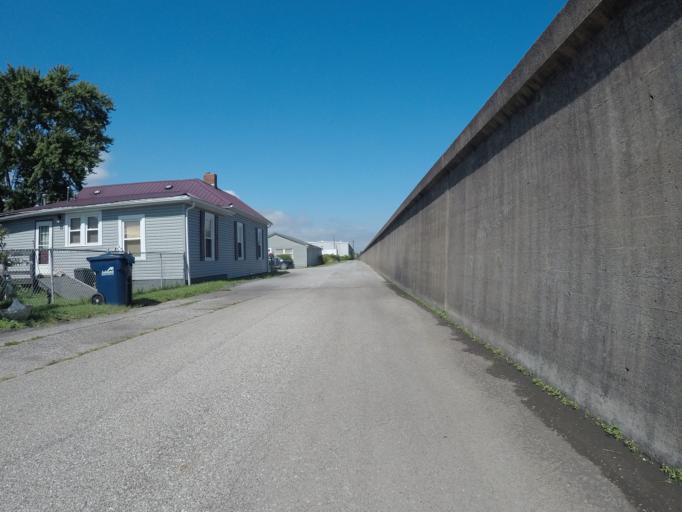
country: US
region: Kentucky
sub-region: Boyd County
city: Ashland
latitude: 38.4706
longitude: -82.6204
